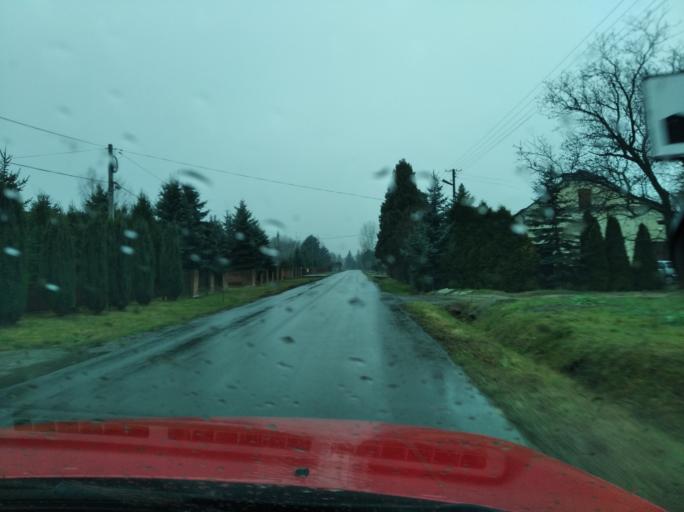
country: PL
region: Subcarpathian Voivodeship
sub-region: Powiat lancucki
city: Krzemienica
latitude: 50.0830
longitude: 22.1557
